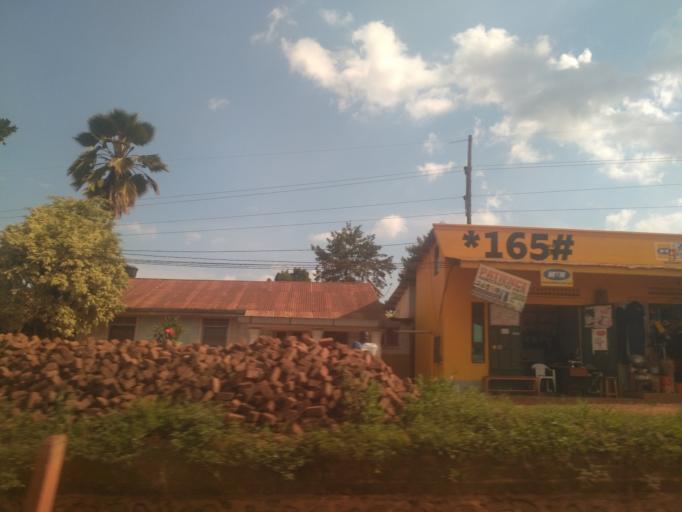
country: UG
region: Central Region
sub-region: Wakiso District
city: Kajansi
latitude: 0.2717
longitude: 32.4643
